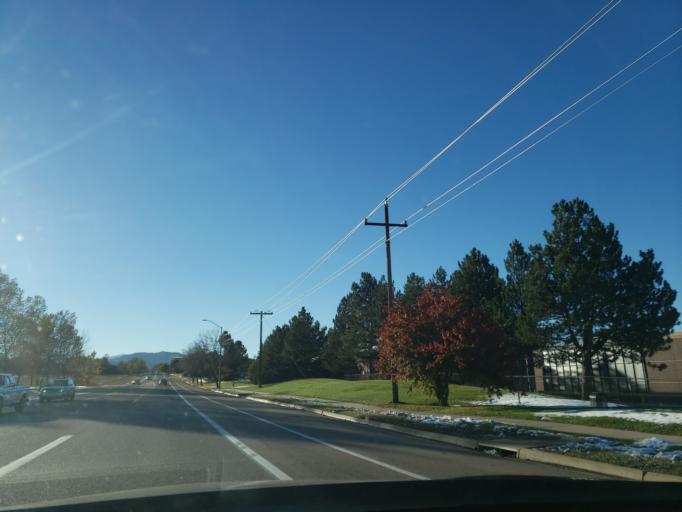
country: US
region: Colorado
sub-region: Larimer County
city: Fort Collins
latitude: 40.4947
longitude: -105.0640
